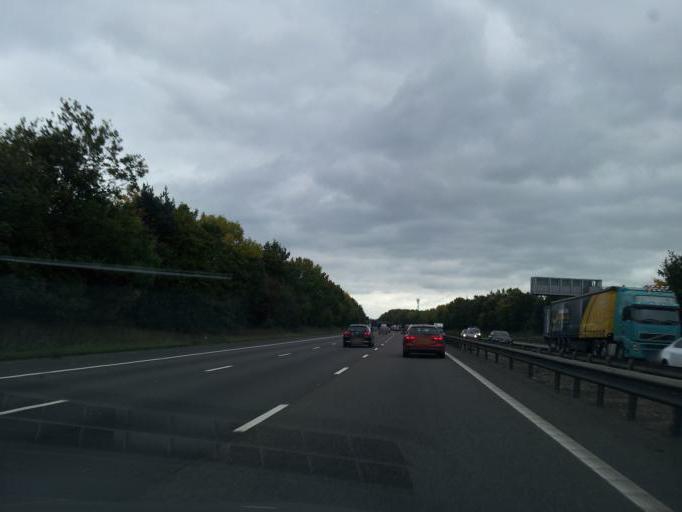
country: GB
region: England
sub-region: Northamptonshire
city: Hartwell
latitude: 52.1386
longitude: -0.8326
